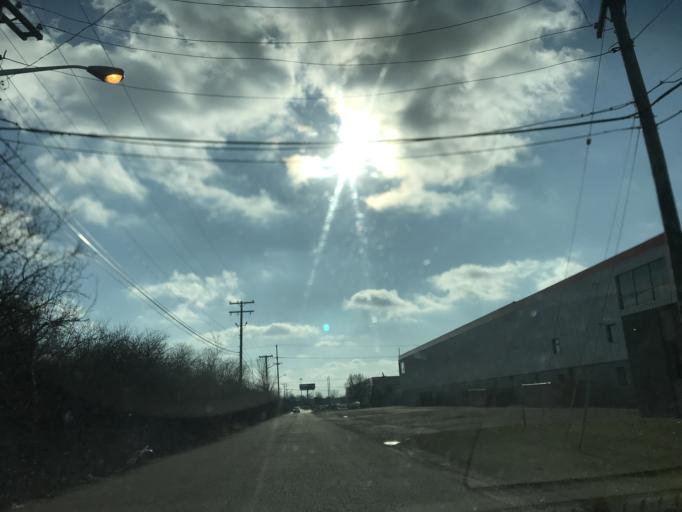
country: US
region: Michigan
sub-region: Oakland County
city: Clawson
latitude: 42.5213
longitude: -83.1162
